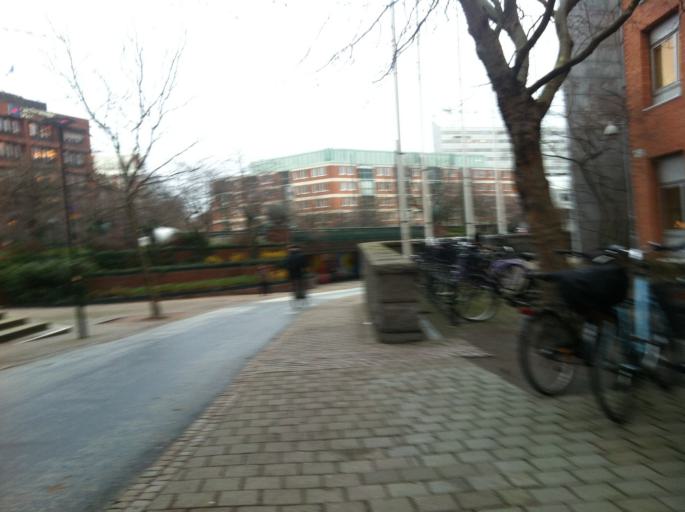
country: SE
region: Skane
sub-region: Malmo
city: Malmoe
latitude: 55.5969
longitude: 13.0069
